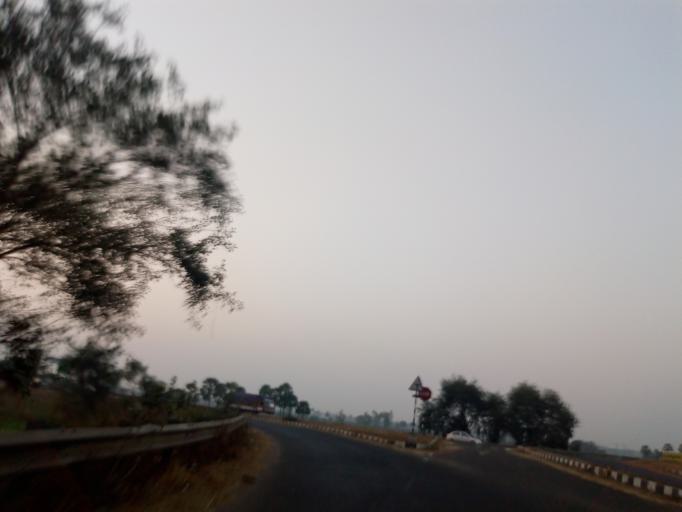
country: IN
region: Andhra Pradesh
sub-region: West Godavari
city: Tadepallegudem
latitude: 16.8242
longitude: 81.4626
